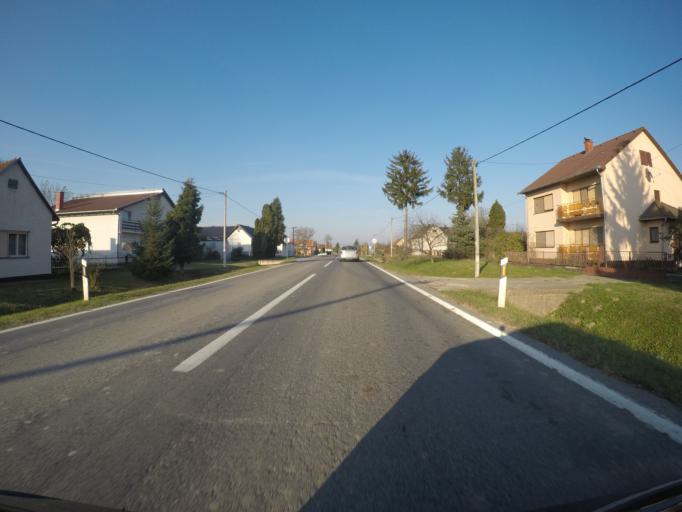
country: HU
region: Somogy
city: Barcs
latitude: 45.9262
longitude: 17.4557
